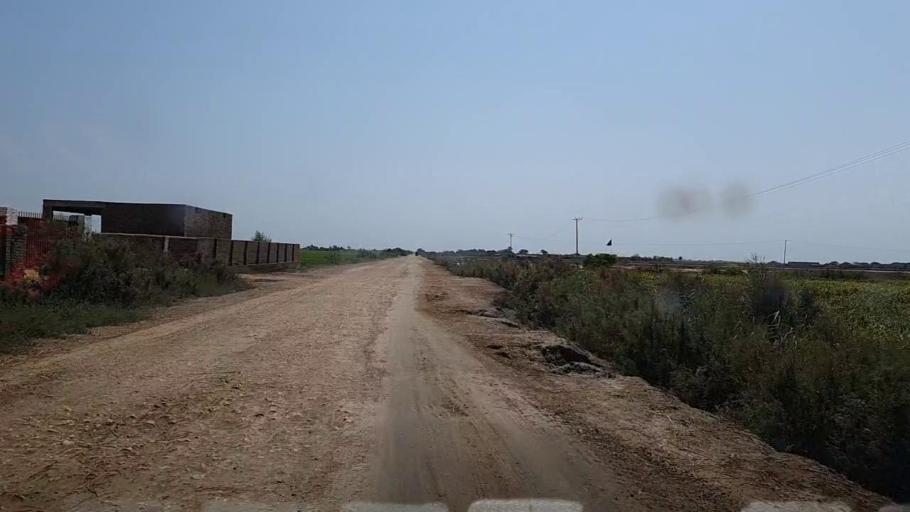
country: PK
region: Sindh
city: Mirpur Batoro
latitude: 24.6350
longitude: 68.4522
